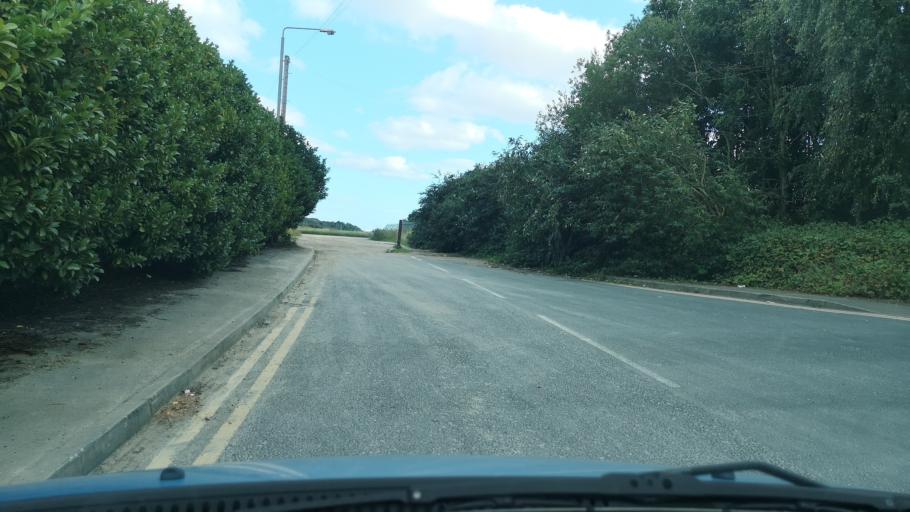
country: GB
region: England
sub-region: City and Borough of Wakefield
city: South Elmsall
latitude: 53.6006
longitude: -1.2675
